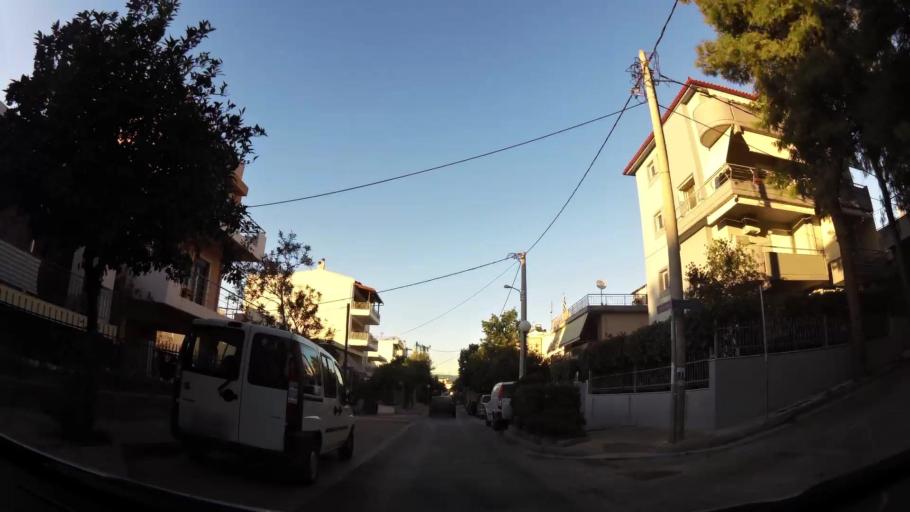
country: GR
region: Attica
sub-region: Nomarchia Athinas
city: Lykovrysi
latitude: 38.0662
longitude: 23.7819
